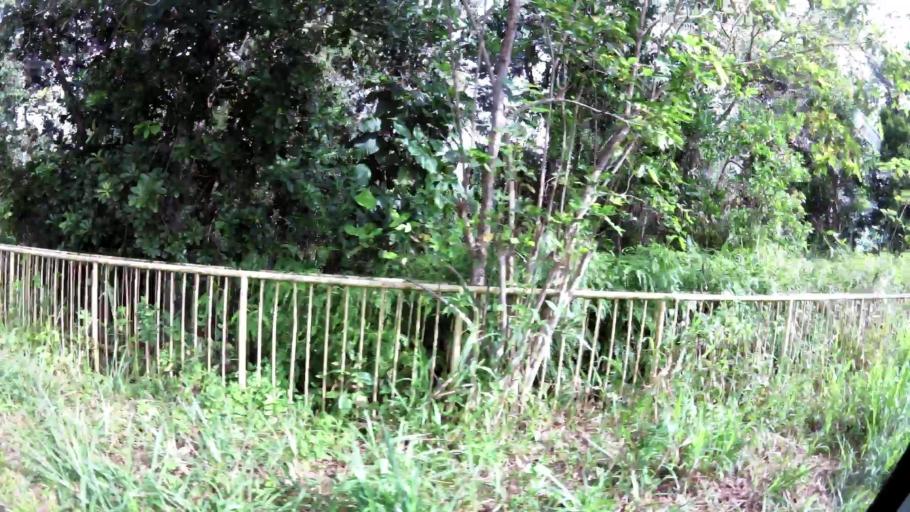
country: BN
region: Brunei and Muara
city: Bandar Seri Begawan
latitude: 4.8954
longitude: 114.8895
